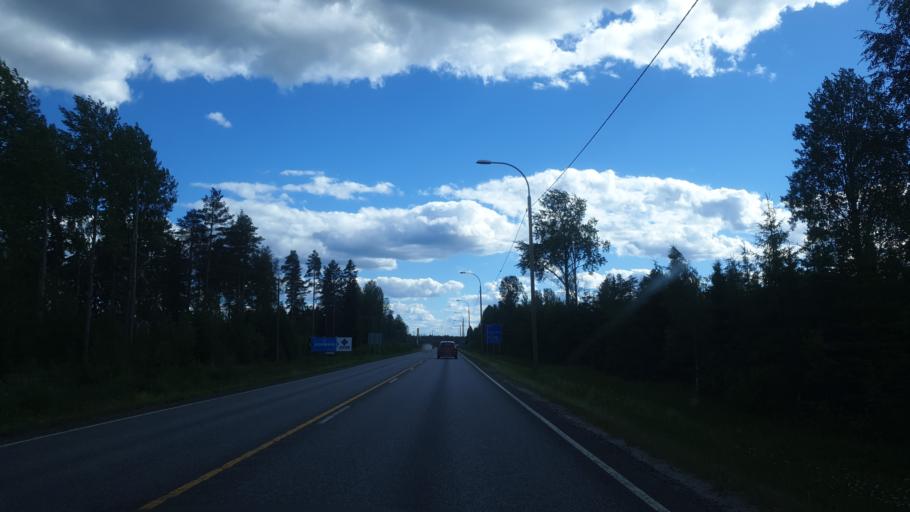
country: FI
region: Southern Savonia
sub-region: Pieksaemaeki
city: Juva
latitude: 61.9075
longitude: 27.8050
